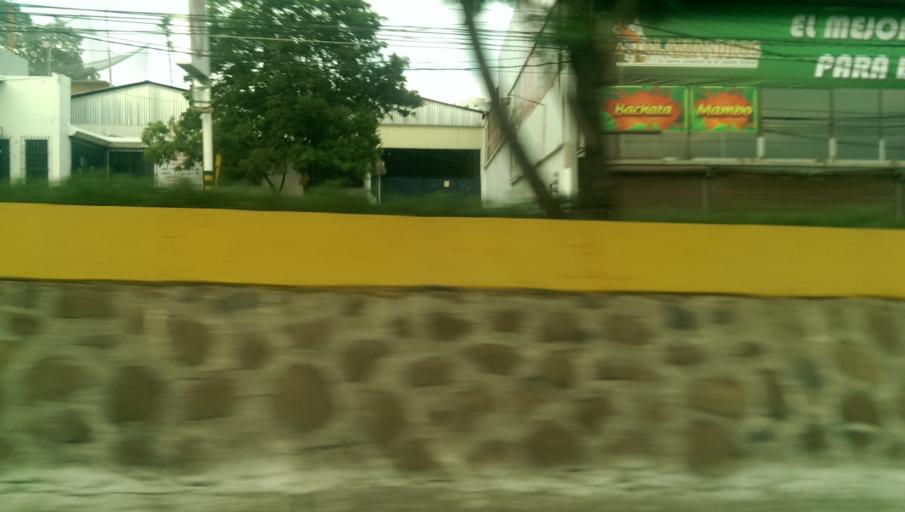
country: MX
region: Queretaro
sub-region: Queretaro
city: Santiago de Queretaro
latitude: 20.5921
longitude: -100.3675
